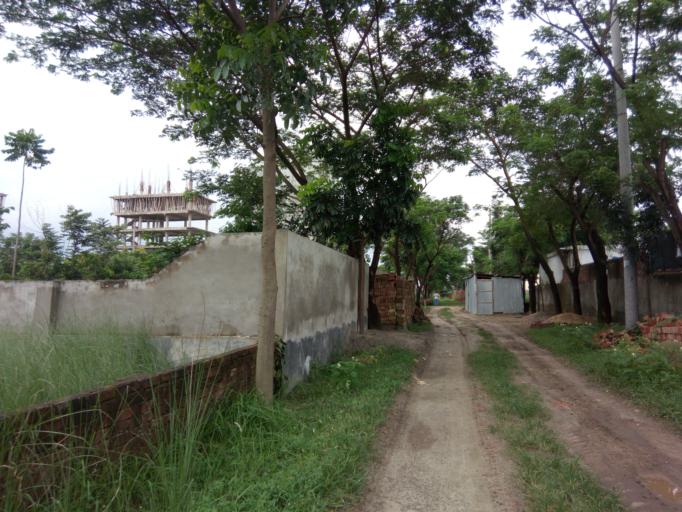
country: BD
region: Dhaka
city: Azimpur
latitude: 23.7484
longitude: 90.3491
